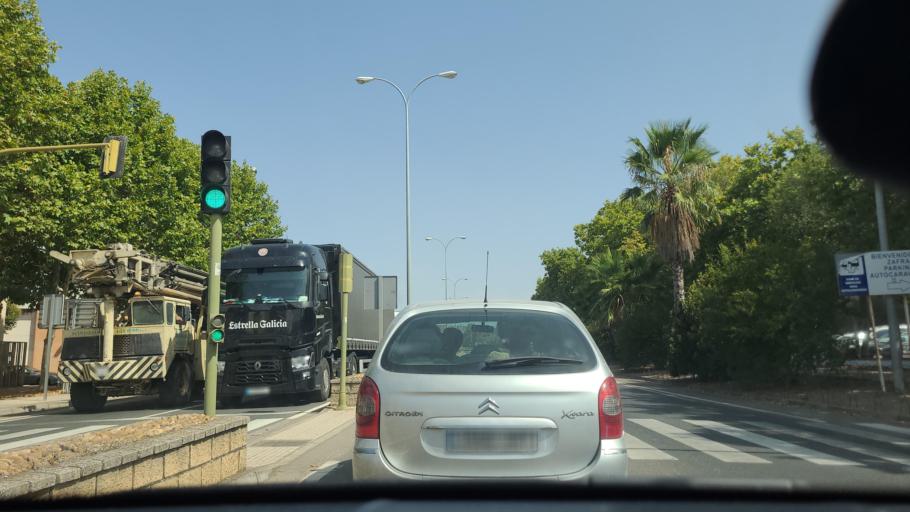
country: ES
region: Extremadura
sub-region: Provincia de Badajoz
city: Zafra
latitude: 38.4248
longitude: -6.4119
